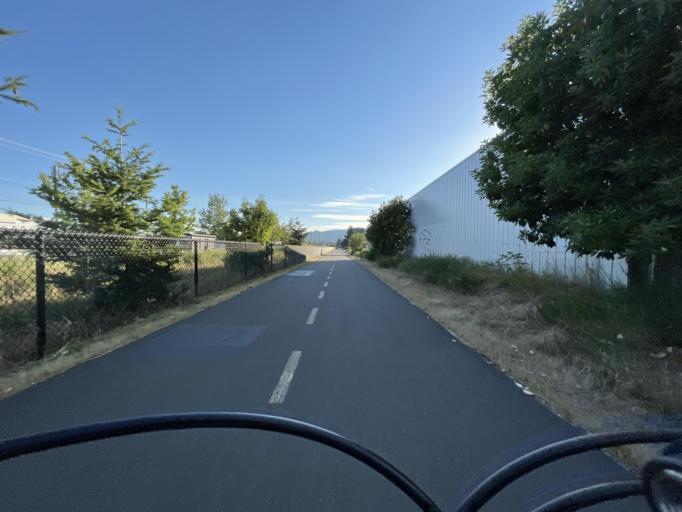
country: CA
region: British Columbia
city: Langford
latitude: 48.4457
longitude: -123.5050
